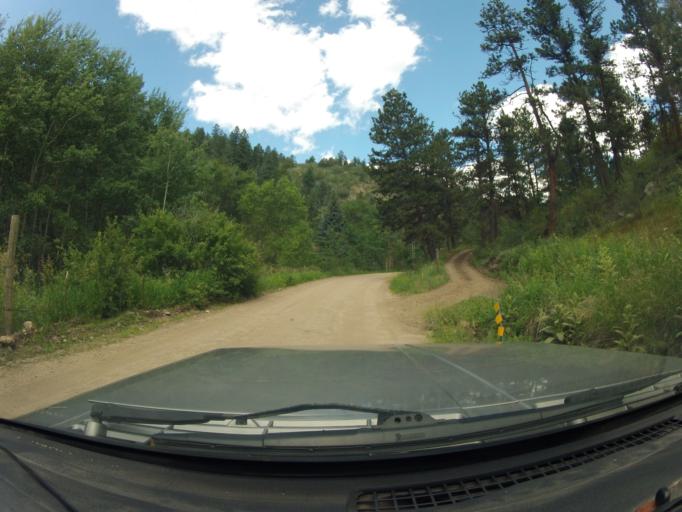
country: US
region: Colorado
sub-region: Larimer County
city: Laporte
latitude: 40.5686
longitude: -105.3421
